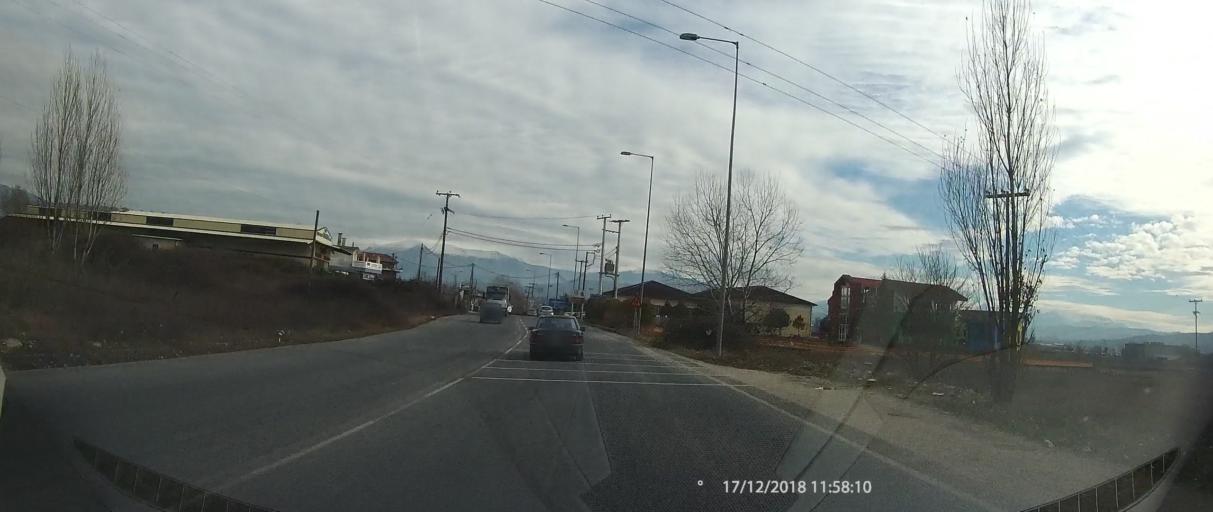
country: GR
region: Epirus
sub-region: Nomos Ioanninon
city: Anatoli
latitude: 39.6220
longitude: 20.8569
